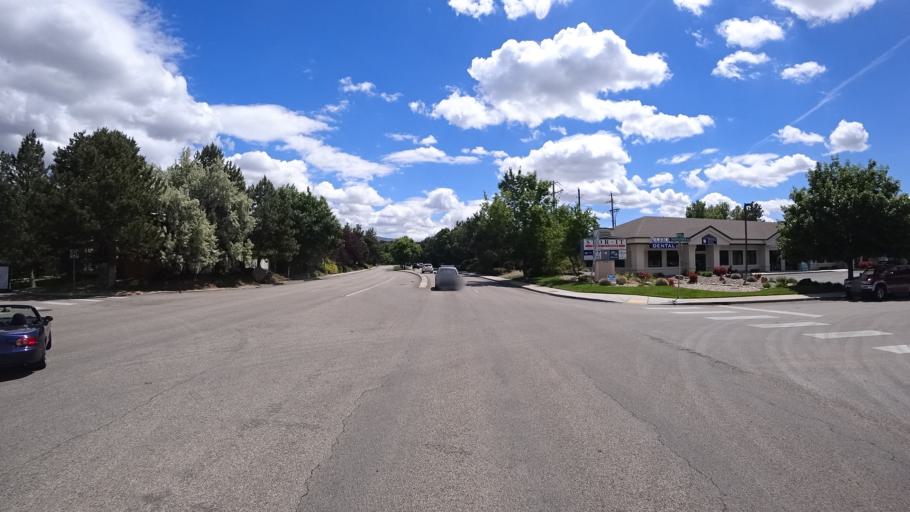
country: US
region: Idaho
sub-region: Ada County
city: Boise
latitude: 43.5823
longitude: -116.1690
